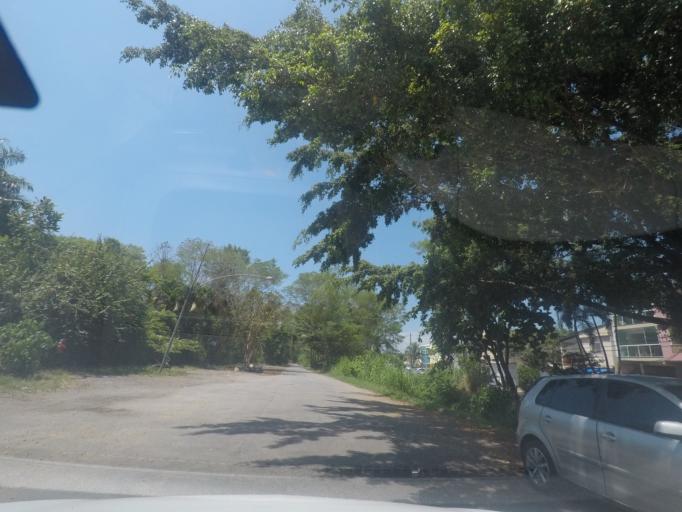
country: BR
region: Rio de Janeiro
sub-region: Nilopolis
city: Nilopolis
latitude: -22.9890
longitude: -43.4553
